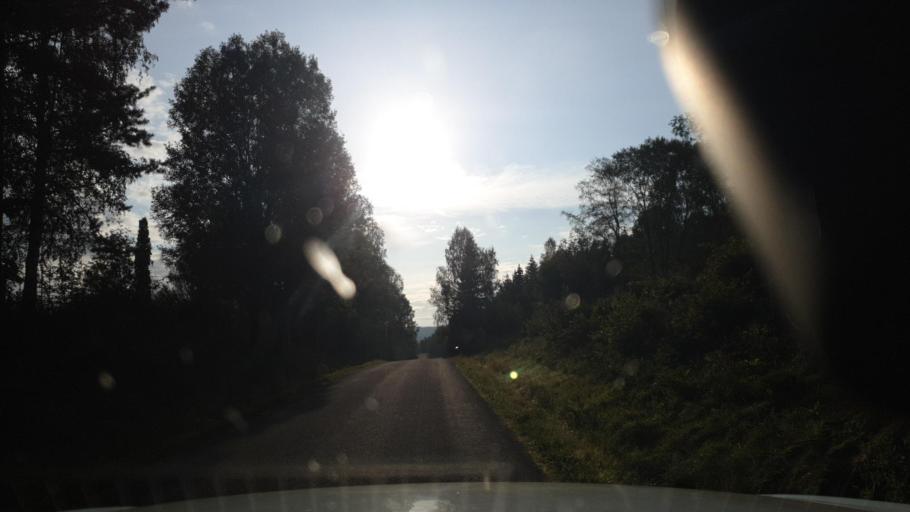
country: SE
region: Vaermland
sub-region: Arvika Kommun
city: Arvika
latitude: 59.7649
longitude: 12.5802
